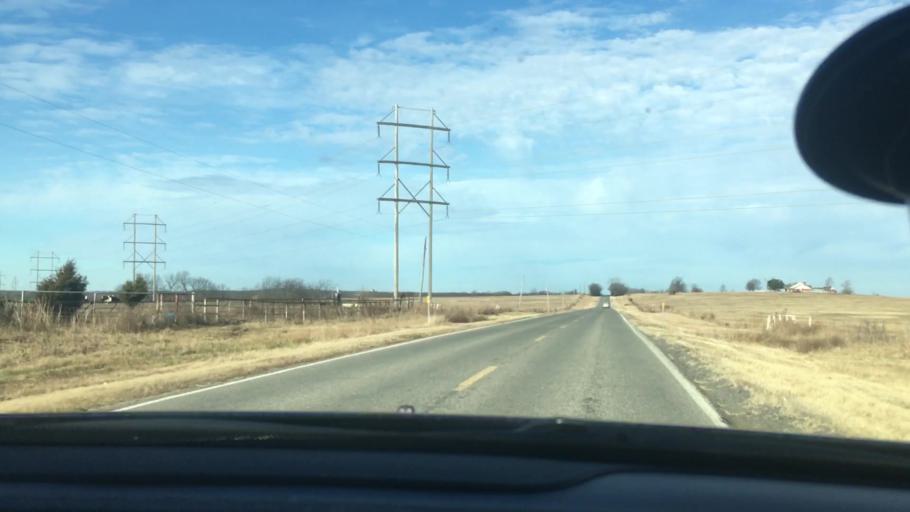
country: US
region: Oklahoma
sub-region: Seminole County
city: Konawa
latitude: 34.9743
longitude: -96.7825
